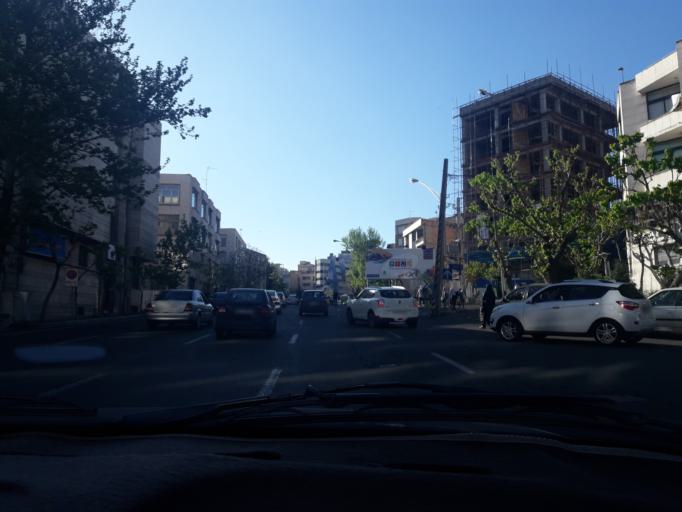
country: IR
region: Tehran
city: Tehran
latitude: 35.7209
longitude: 51.4028
